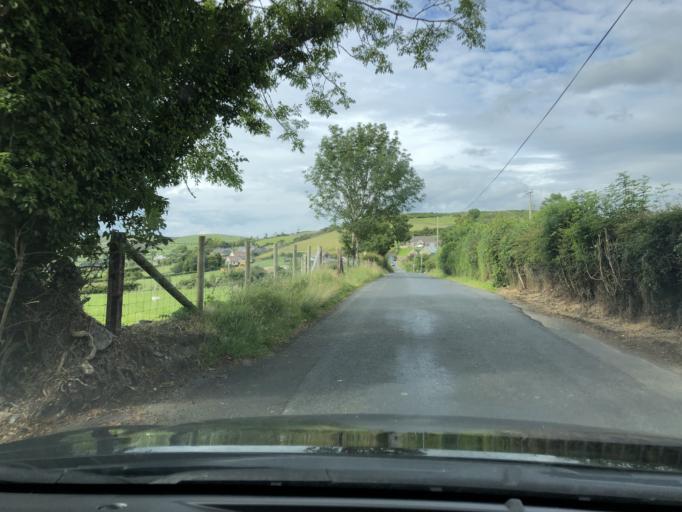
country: GB
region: Northern Ireland
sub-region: Down District
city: Castlewellan
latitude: 54.2281
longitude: -6.0126
